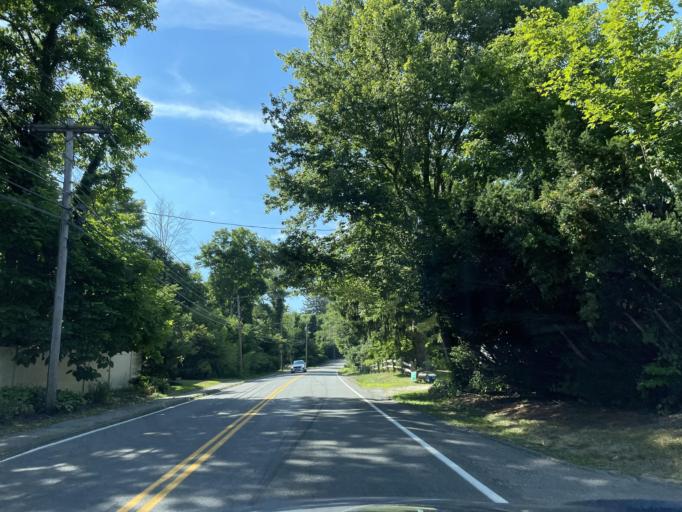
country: US
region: Massachusetts
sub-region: Worcester County
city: Mendon
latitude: 42.1133
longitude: -71.5592
